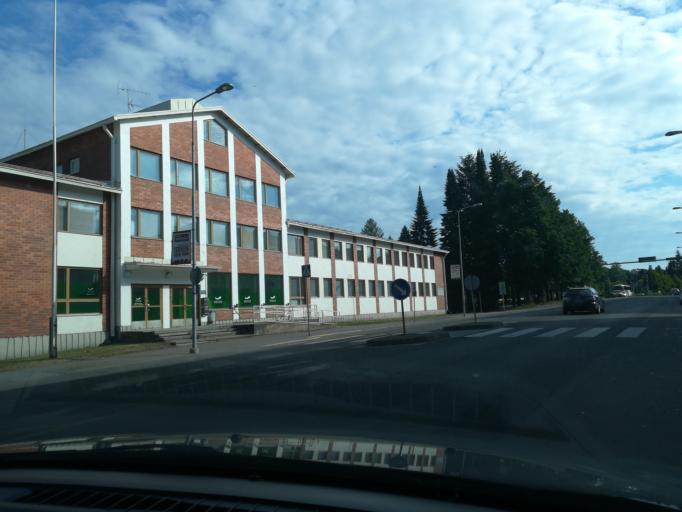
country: FI
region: South Karelia
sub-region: Imatra
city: Imatra
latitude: 61.1717
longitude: 28.7734
